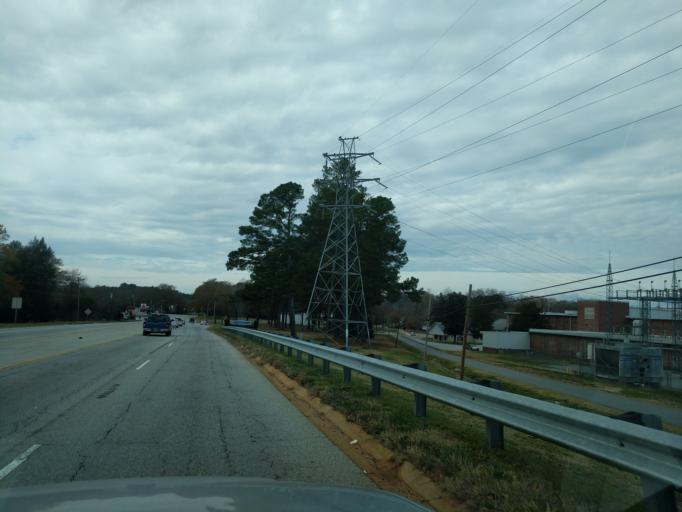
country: US
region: South Carolina
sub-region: Pickens County
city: Arial
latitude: 34.8421
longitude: -82.6406
